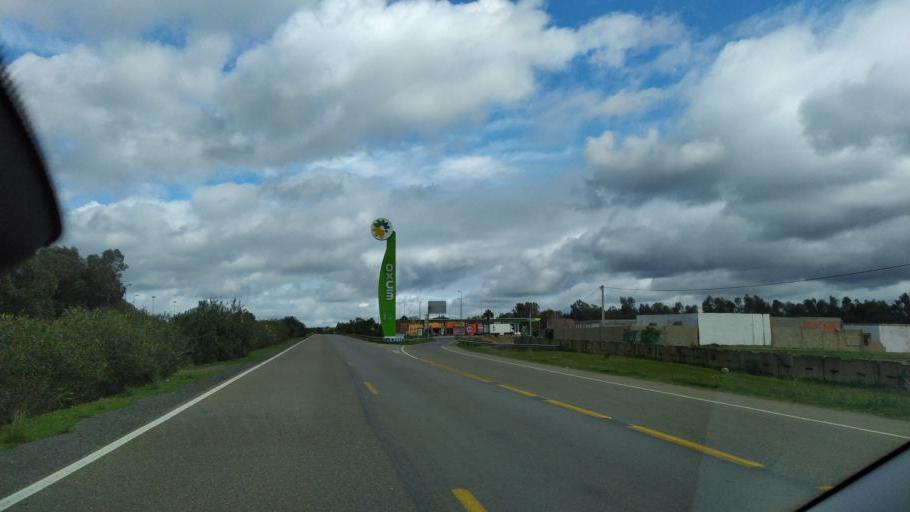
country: MA
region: Gharb-Chrarda-Beni Hssen
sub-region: Kenitra Province
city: Lalla Mimouna
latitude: 34.8734
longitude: -6.2154
